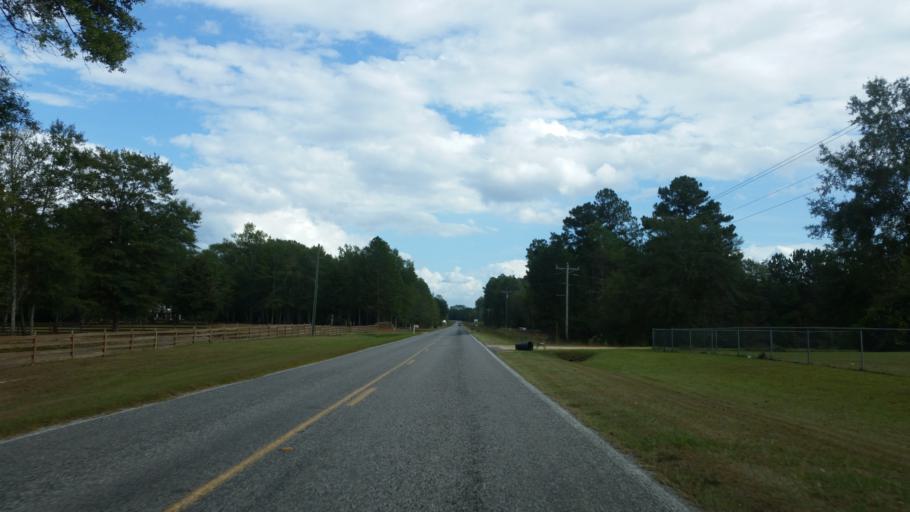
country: US
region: Mississippi
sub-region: Stone County
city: Wiggins
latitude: 30.9122
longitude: -89.0991
